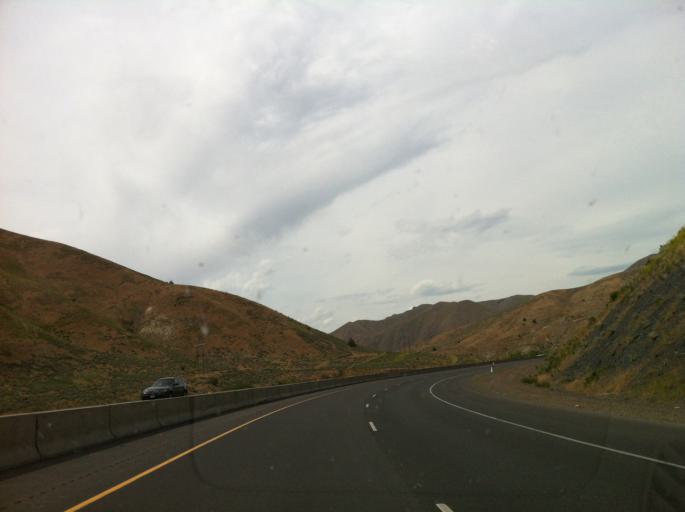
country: US
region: Idaho
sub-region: Washington County
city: Weiser
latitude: 44.4172
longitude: -117.3094
